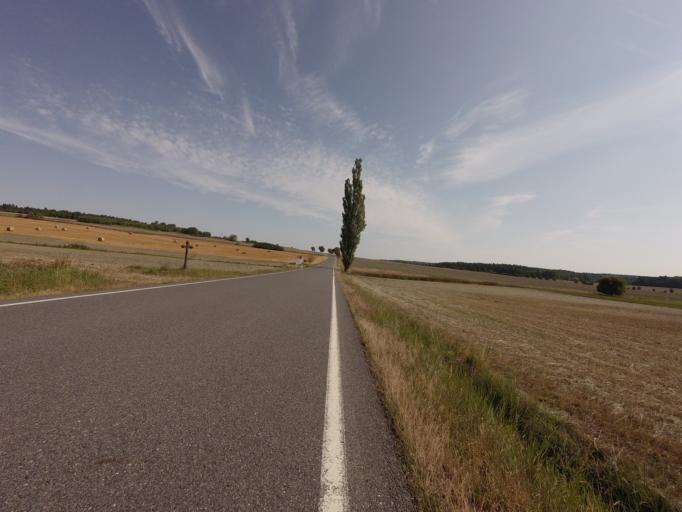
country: CZ
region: Jihocesky
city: Bernartice
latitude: 49.3468
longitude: 14.3705
